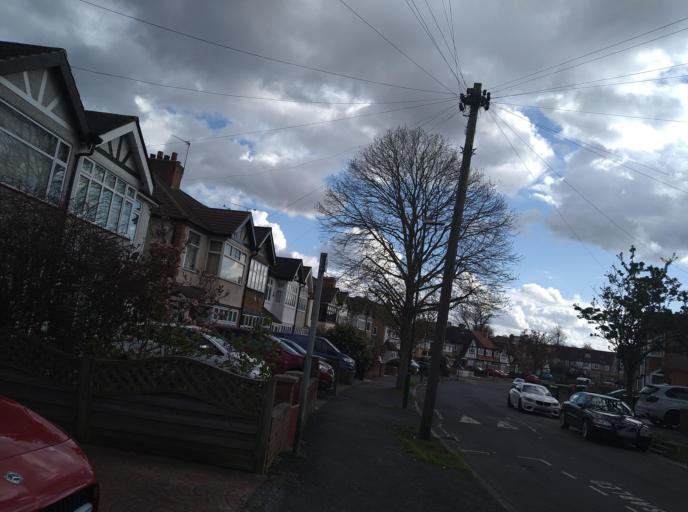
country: GB
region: England
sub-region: Greater London
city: Carshalton
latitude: 51.3742
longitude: -0.1831
